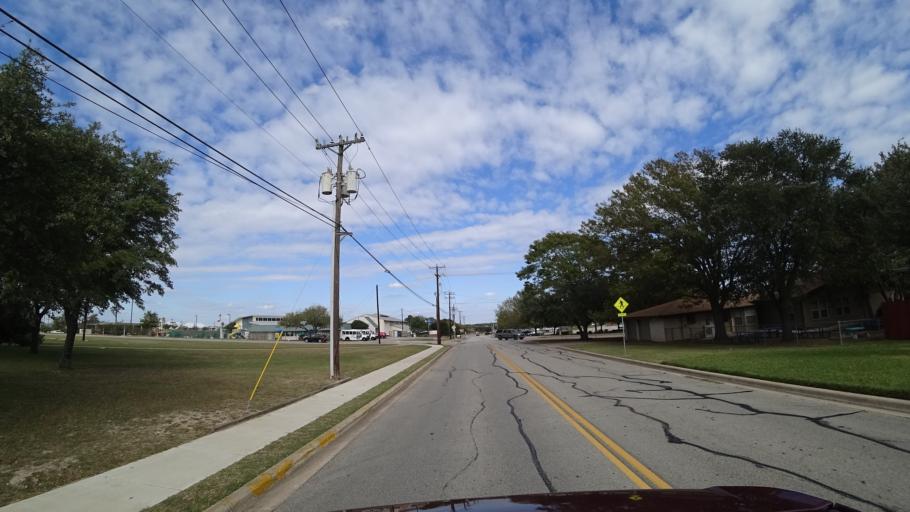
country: US
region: Texas
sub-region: Travis County
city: Pflugerville
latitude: 30.4411
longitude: -97.6289
